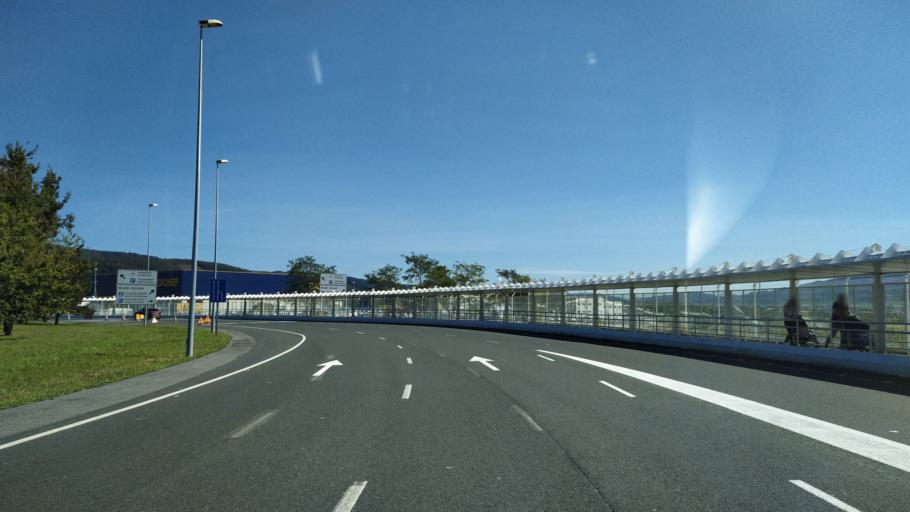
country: ES
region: Basque Country
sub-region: Bizkaia
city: Sondika
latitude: 43.3046
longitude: -2.9037
